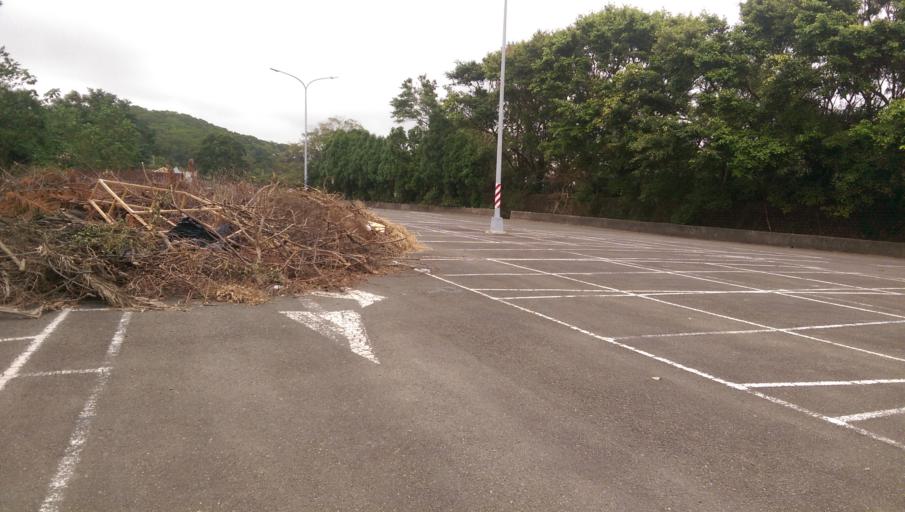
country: TW
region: Taiwan
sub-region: Hsinchu
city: Hsinchu
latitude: 24.7607
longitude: 120.9509
